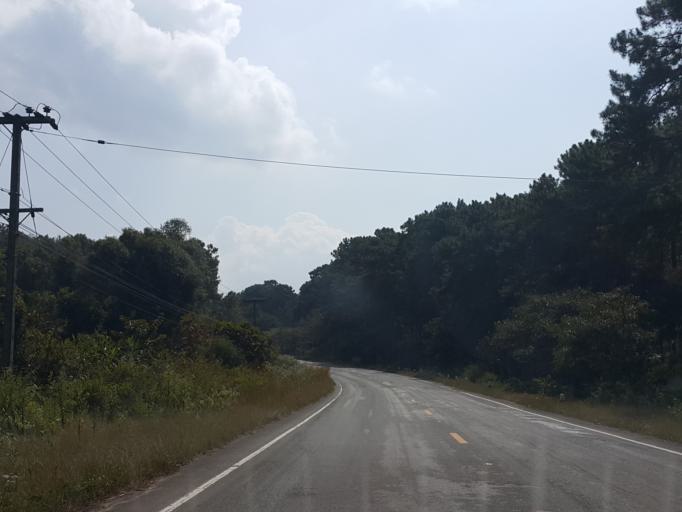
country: TH
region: Chiang Mai
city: Hot
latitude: 18.1221
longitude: 98.3765
